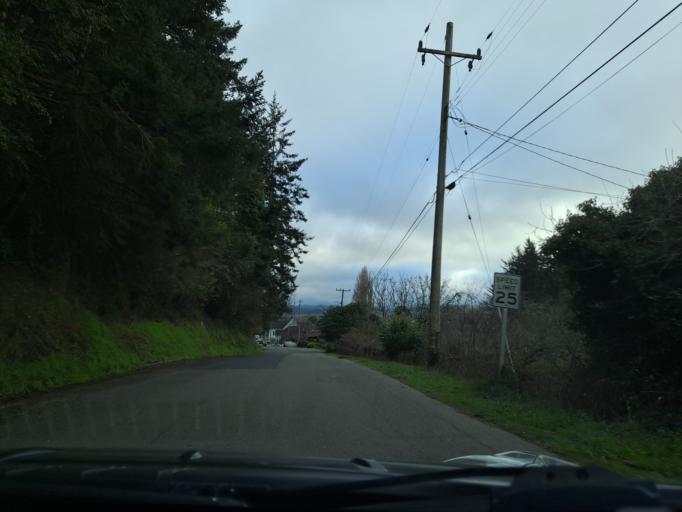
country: US
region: California
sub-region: Humboldt County
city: Fortuna
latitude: 40.6024
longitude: -124.1575
